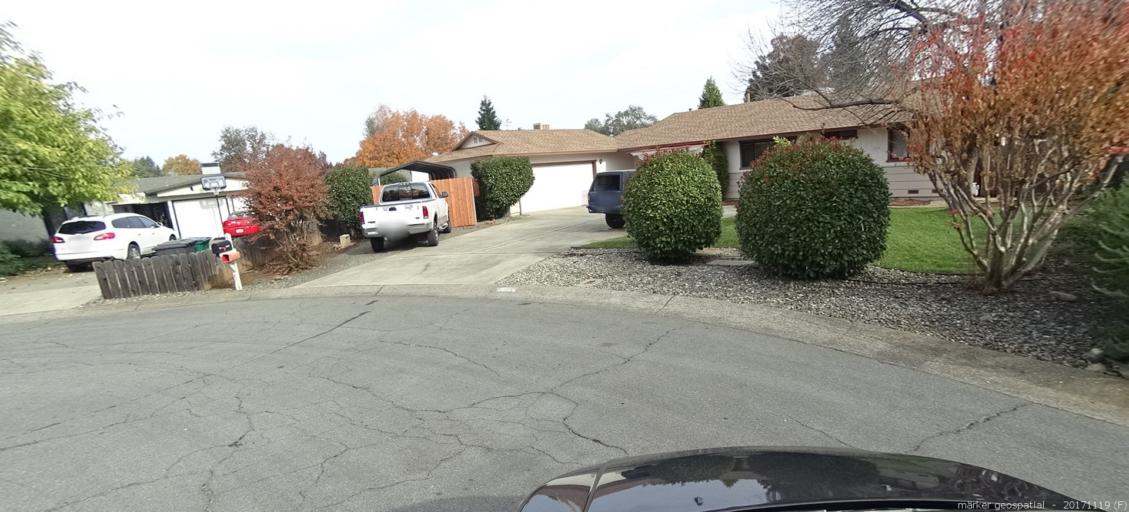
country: US
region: California
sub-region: Shasta County
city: Anderson
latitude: 40.4901
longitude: -122.3065
